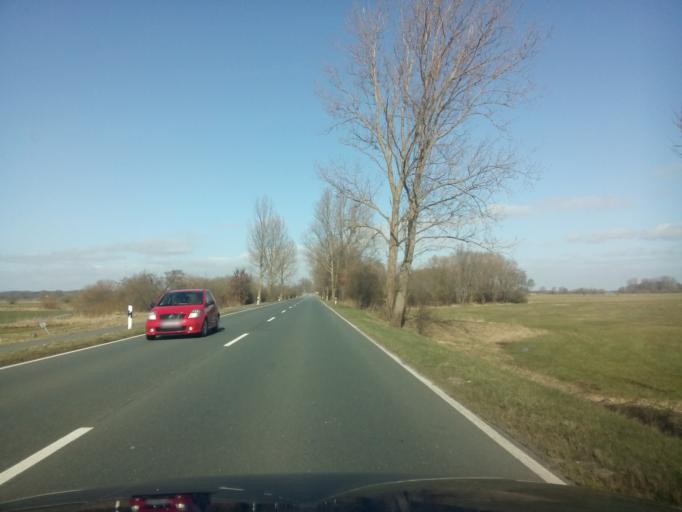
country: DE
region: Lower Saxony
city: Osterholz-Scharmbeck
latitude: 53.1969
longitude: 8.8209
